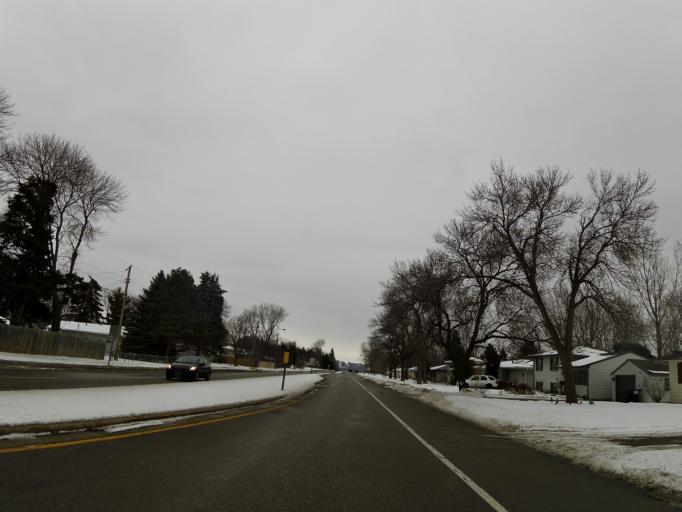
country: US
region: Minnesota
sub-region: Dakota County
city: Inver Grove Heights
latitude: 44.8480
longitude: -93.0271
